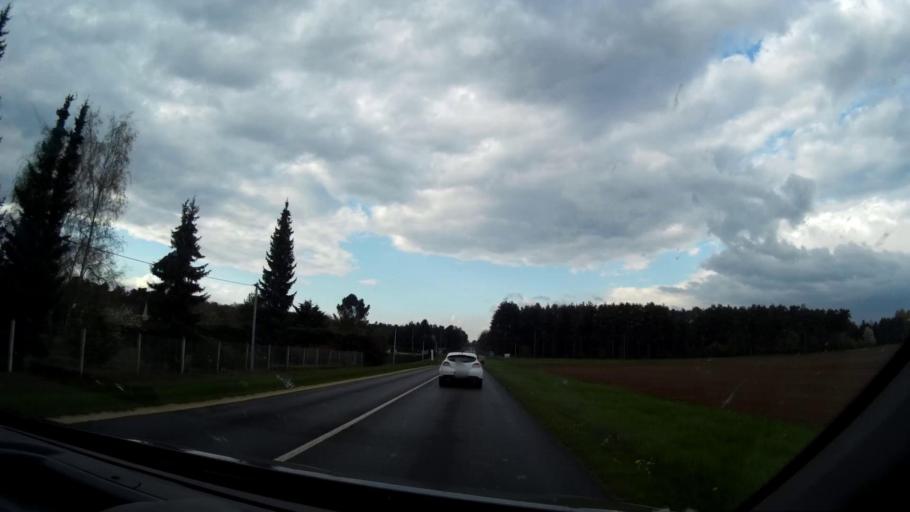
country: FR
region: Centre
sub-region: Departement du Loir-et-Cher
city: Contres
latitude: 47.4533
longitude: 1.4258
